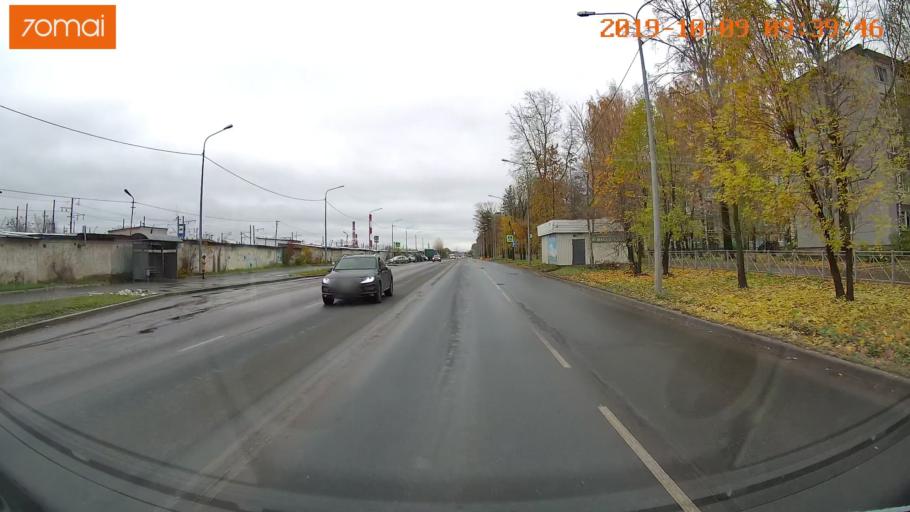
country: RU
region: Vologda
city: Vologda
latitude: 59.1978
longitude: 39.9155
